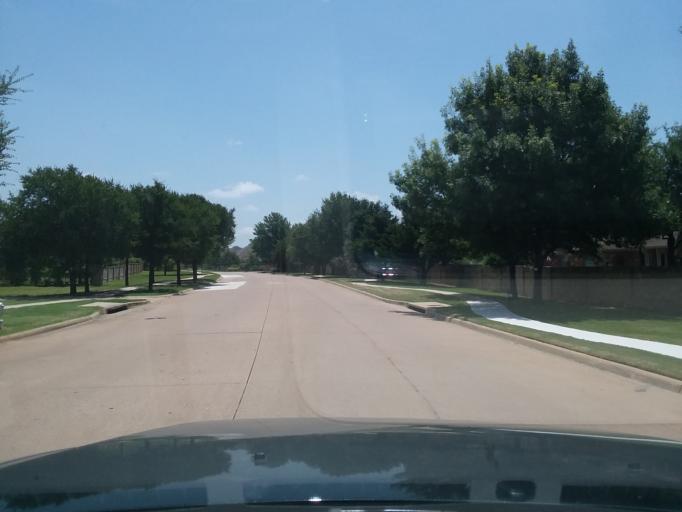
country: US
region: Texas
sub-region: Denton County
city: Bartonville
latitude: 33.0933
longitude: -97.1277
